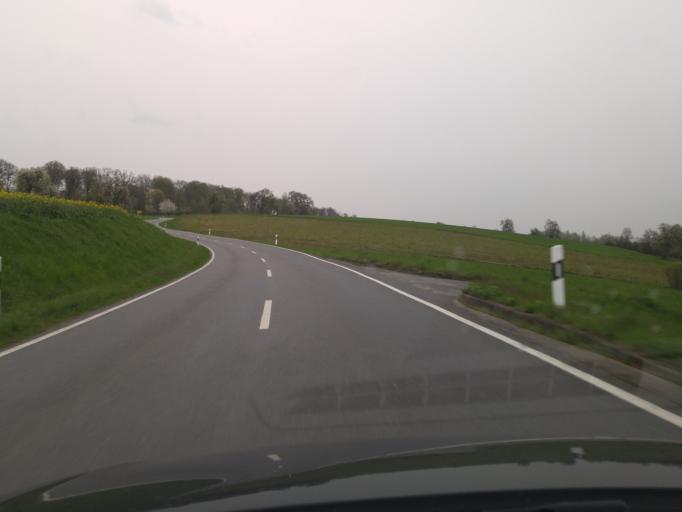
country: DE
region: Baden-Wuerttemberg
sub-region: Karlsruhe Region
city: Aglasterhausen
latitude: 49.3669
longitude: 8.9670
